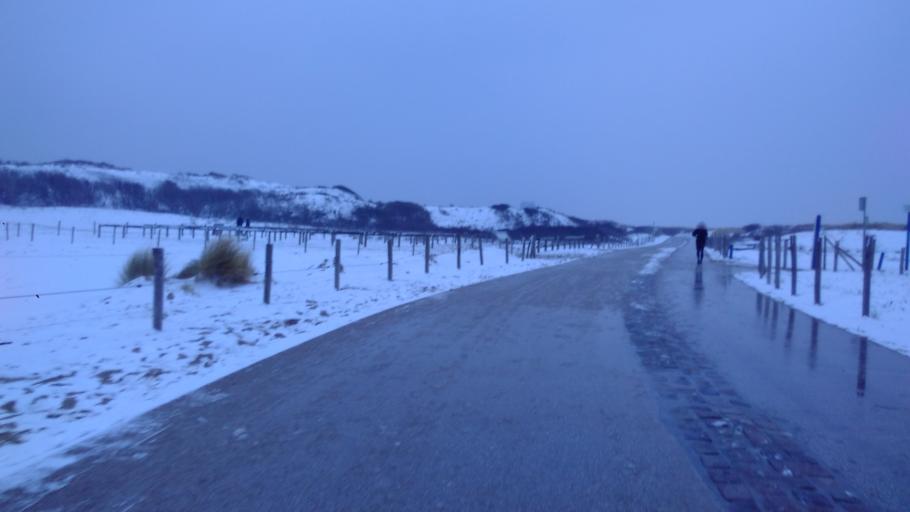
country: NL
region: South Holland
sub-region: Gemeente Den Haag
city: Scheveningen
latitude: 52.0766
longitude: 4.2310
